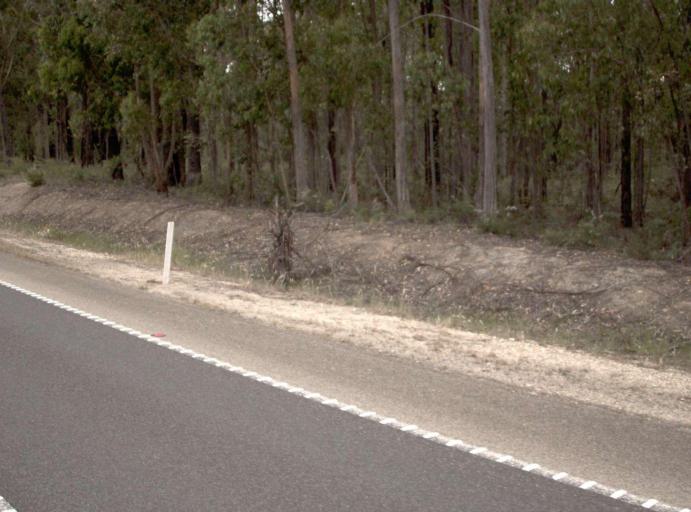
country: AU
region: Victoria
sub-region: East Gippsland
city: Lakes Entrance
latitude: -37.6898
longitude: 148.0301
